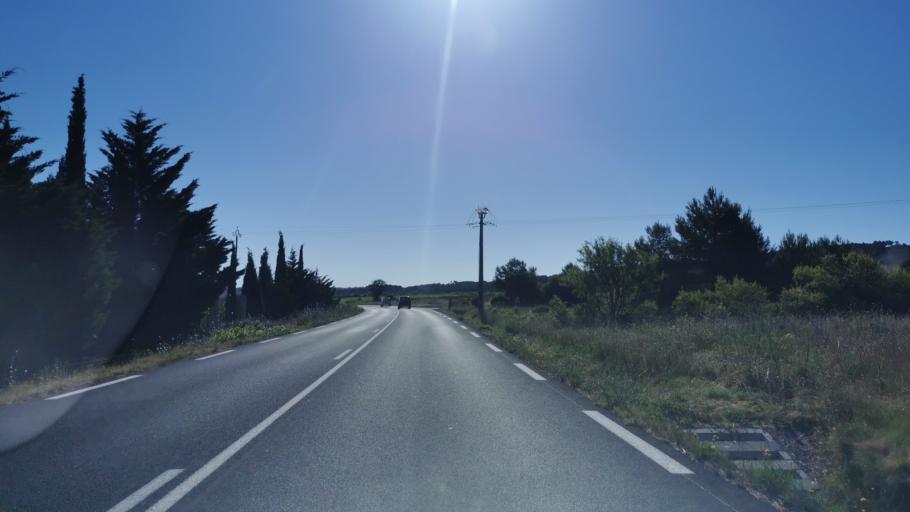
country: FR
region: Languedoc-Roussillon
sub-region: Departement de l'Herault
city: Nissan-lez-Enserune
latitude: 43.2770
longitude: 3.0912
